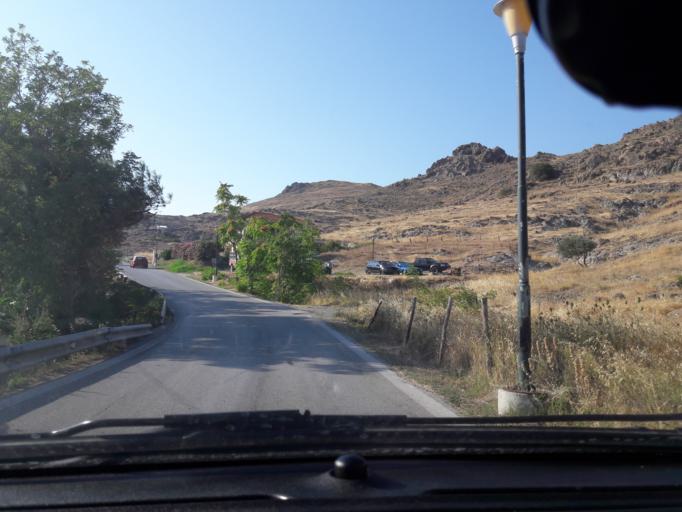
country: GR
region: North Aegean
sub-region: Nomos Lesvou
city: Myrina
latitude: 39.8577
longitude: 25.0841
